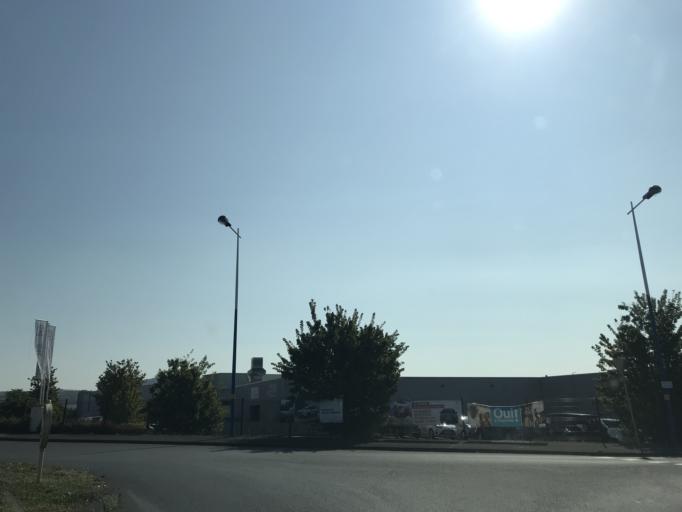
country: FR
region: Auvergne
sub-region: Departement du Puy-de-Dome
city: Perignat-les-Sarlieve
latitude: 45.7521
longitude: 3.1385
